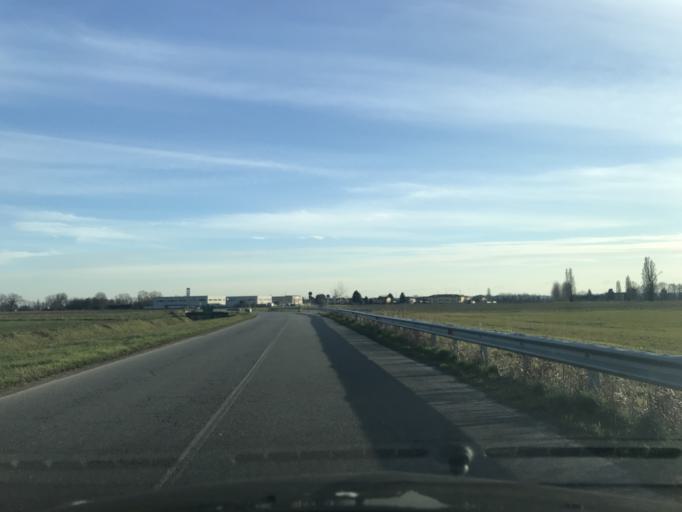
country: IT
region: Lombardy
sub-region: Provincia di Lodi
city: Bargano
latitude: 45.2469
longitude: 9.4391
